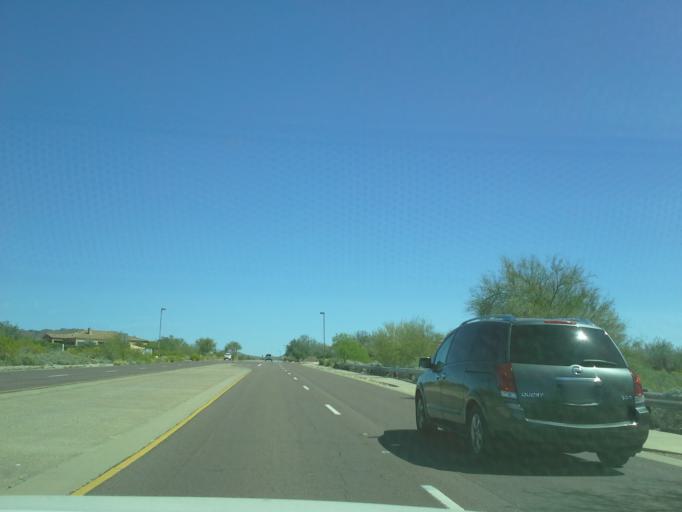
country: US
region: Arizona
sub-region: Maricopa County
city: Fountain Hills
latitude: 33.5896
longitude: -111.8234
